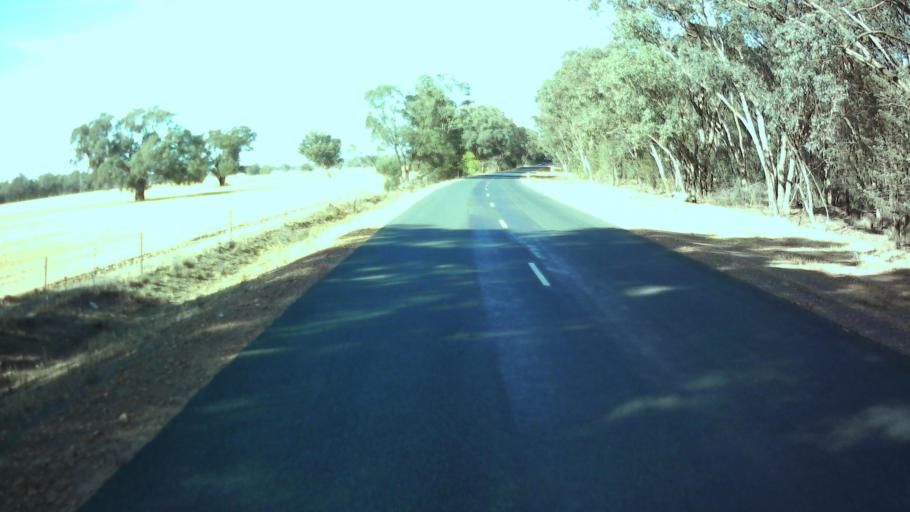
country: AU
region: New South Wales
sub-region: Weddin
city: Grenfell
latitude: -34.0099
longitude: 148.1196
